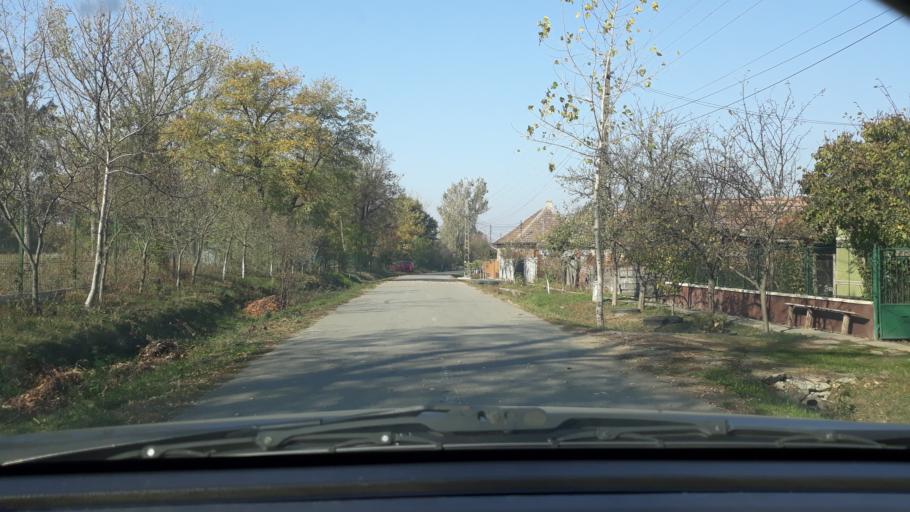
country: RO
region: Bihor
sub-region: Comuna Tarcea
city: Galospetreu
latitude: 47.4835
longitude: 22.2155
